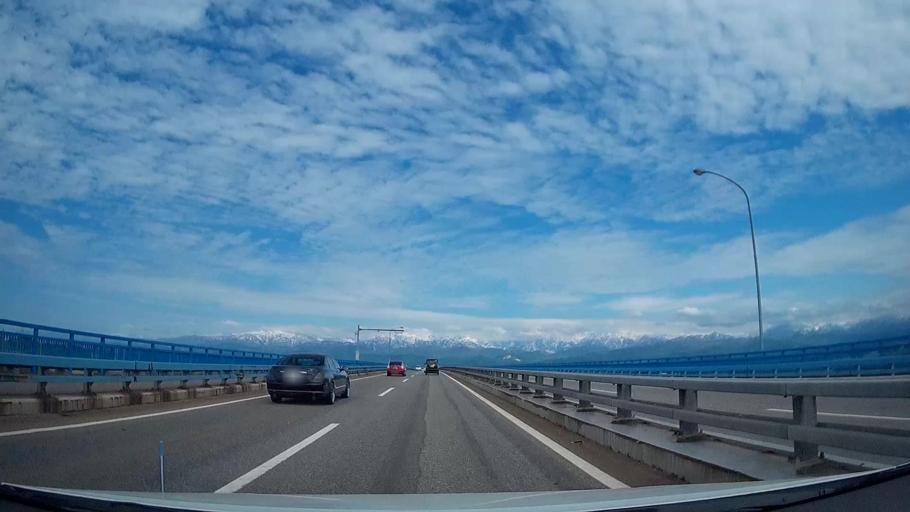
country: JP
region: Toyama
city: Toyama-shi
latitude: 36.7187
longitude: 137.2724
